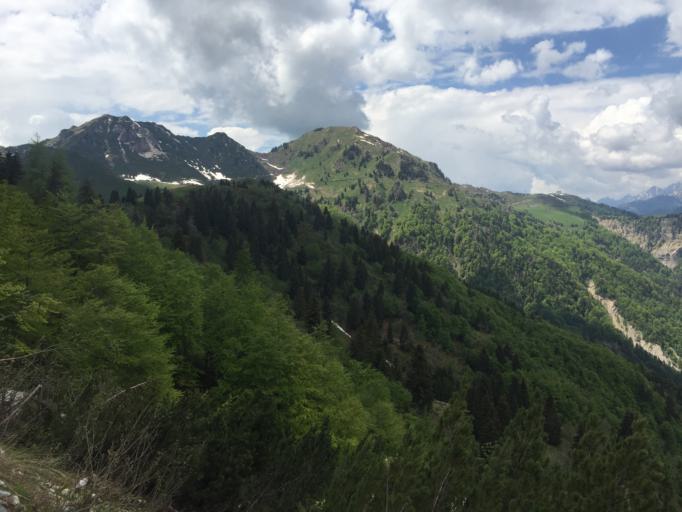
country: IT
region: Friuli Venezia Giulia
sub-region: Provincia di Udine
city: Sutrio
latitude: 46.4802
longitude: 12.9680
